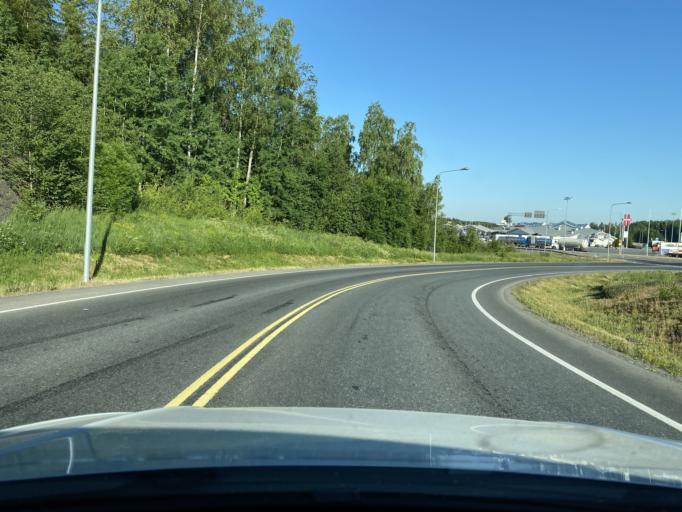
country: FI
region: Haeme
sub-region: Forssa
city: Forssa
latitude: 60.8245
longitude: 23.5821
